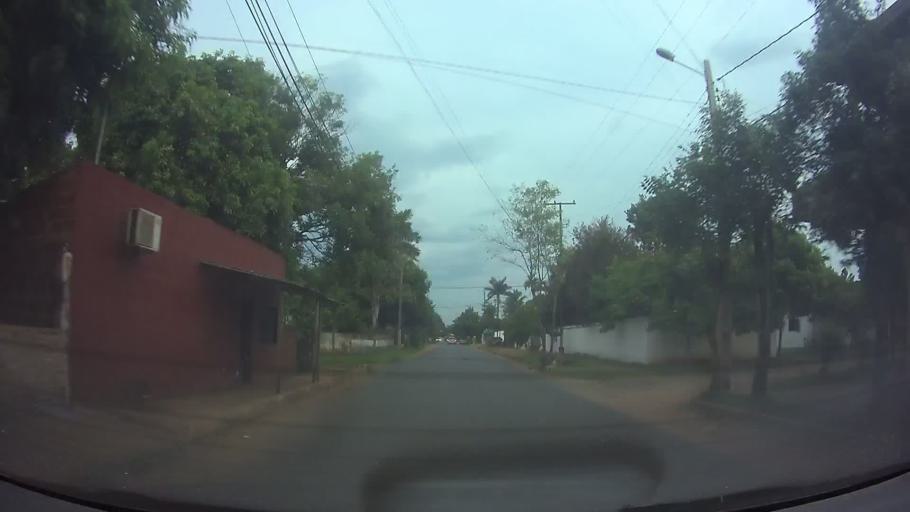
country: PY
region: Central
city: San Lorenzo
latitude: -25.2711
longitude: -57.4693
